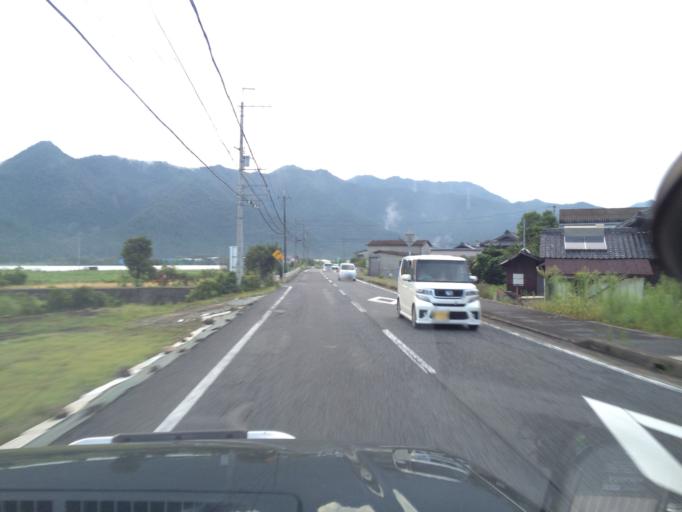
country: JP
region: Hyogo
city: Nishiwaki
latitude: 35.1026
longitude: 134.9954
